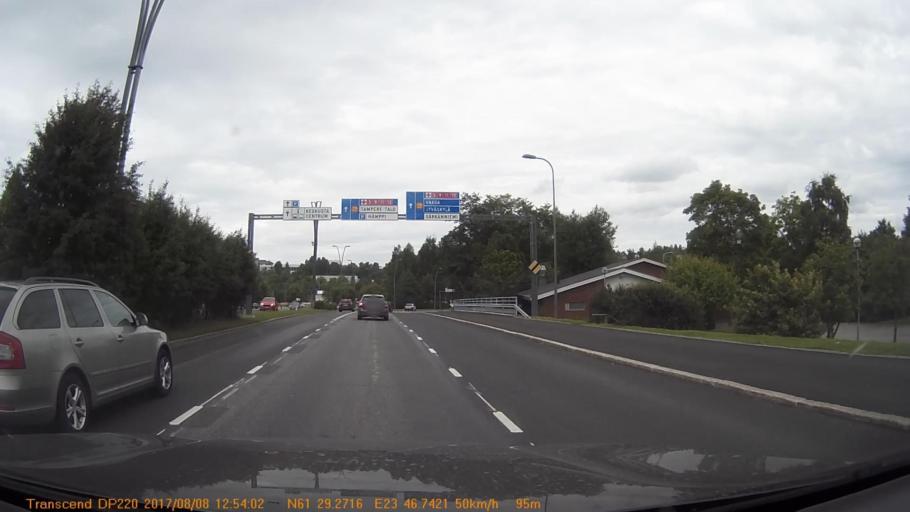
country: FI
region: Pirkanmaa
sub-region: Tampere
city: Tampere
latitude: 61.4880
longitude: 23.7792
